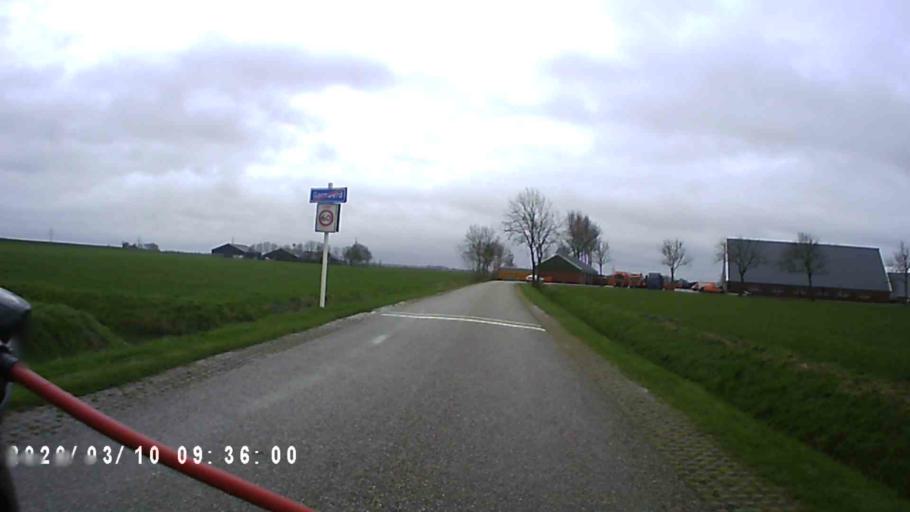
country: NL
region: Groningen
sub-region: Gemeente Winsum
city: Winsum
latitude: 53.3013
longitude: 6.4933
